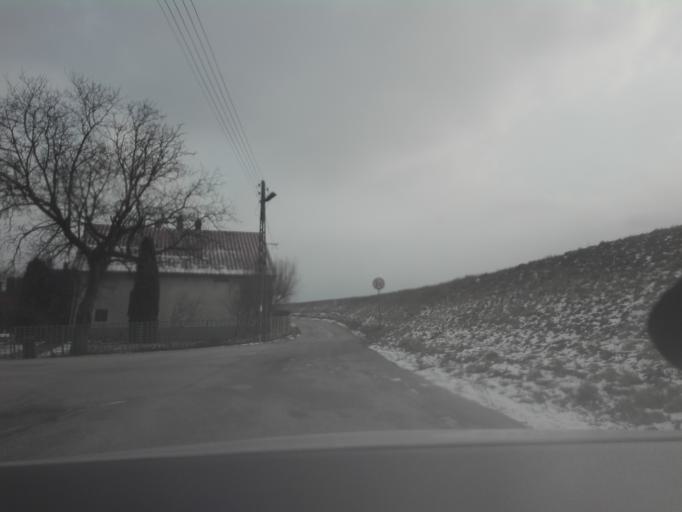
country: PL
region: Subcarpathian Voivodeship
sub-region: Powiat tarnobrzeski
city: Sokolniki
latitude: 50.6546
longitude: 21.7807
